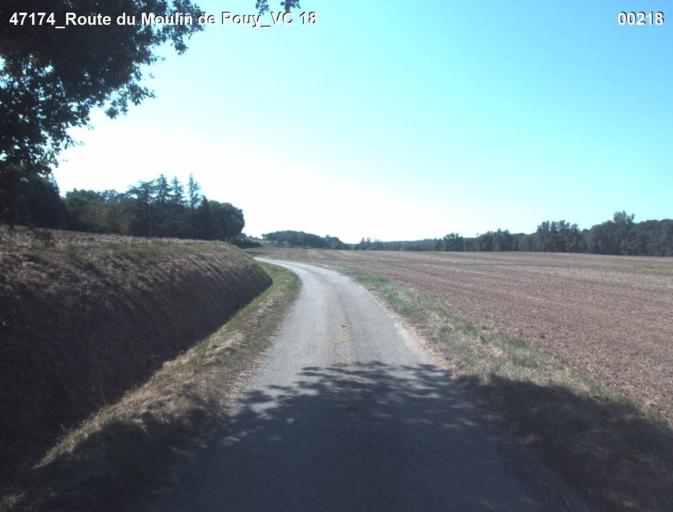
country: FR
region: Aquitaine
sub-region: Departement du Lot-et-Garonne
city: Mezin
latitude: 44.0622
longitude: 0.3190
